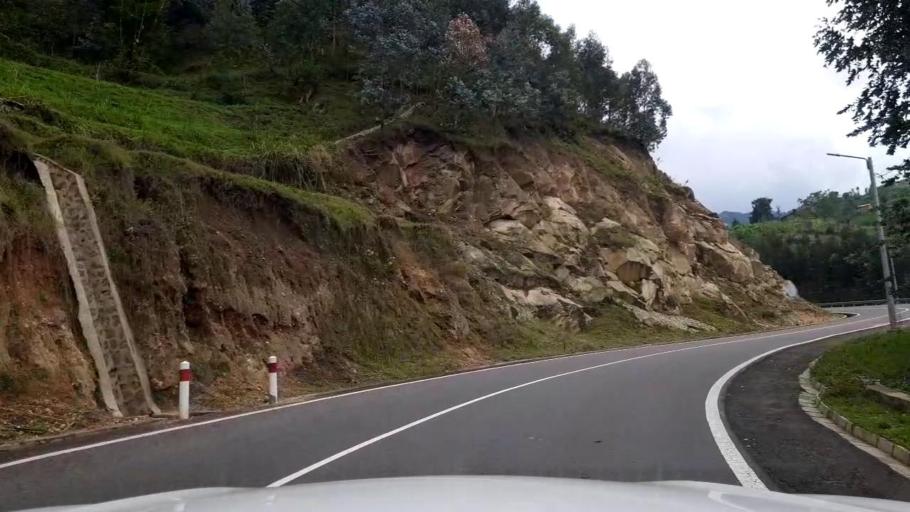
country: RW
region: Western Province
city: Kibuye
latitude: -1.9309
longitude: 29.3752
